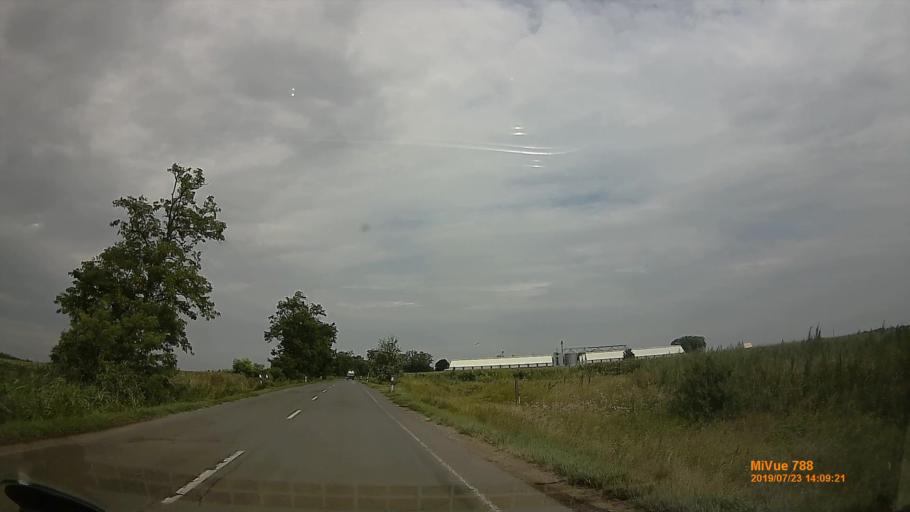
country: HU
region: Szabolcs-Szatmar-Bereg
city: Tiszavasvari
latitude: 47.9580
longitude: 21.3954
